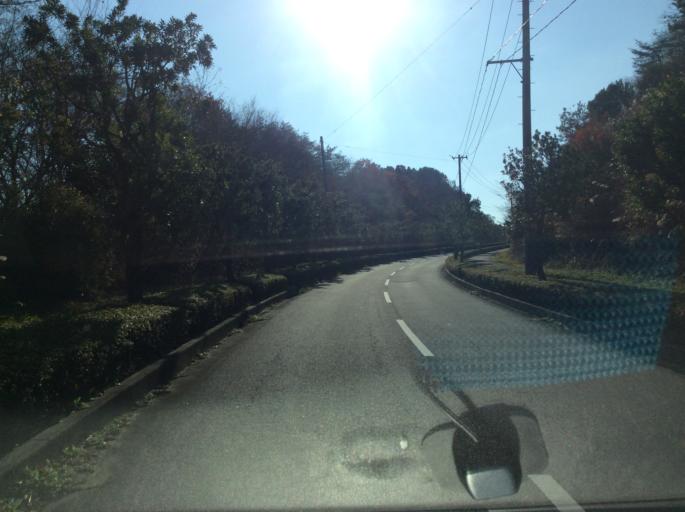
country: JP
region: Fukushima
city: Iwaki
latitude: 37.0206
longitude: 140.9243
